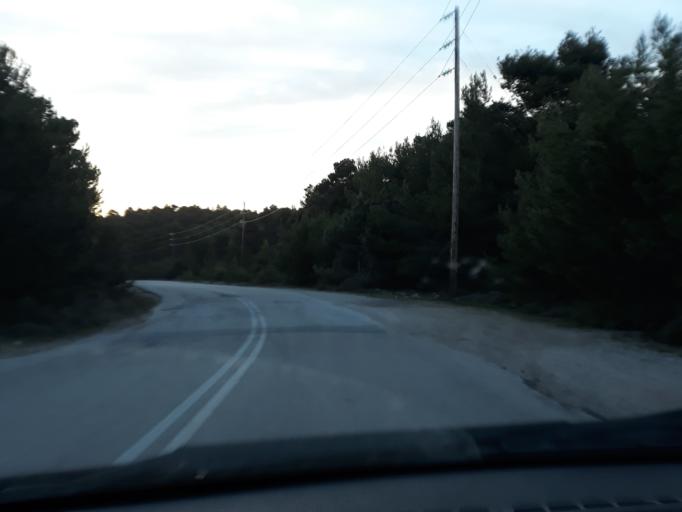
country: GR
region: Attica
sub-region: Nomarchia Anatolikis Attikis
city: Afidnes
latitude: 38.2116
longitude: 23.8047
